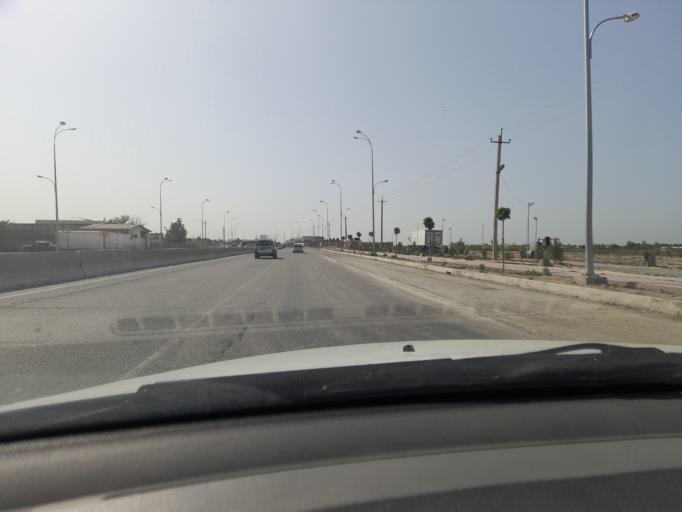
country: UZ
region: Samarqand
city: Samarqand
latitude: 39.7106
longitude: 66.9786
